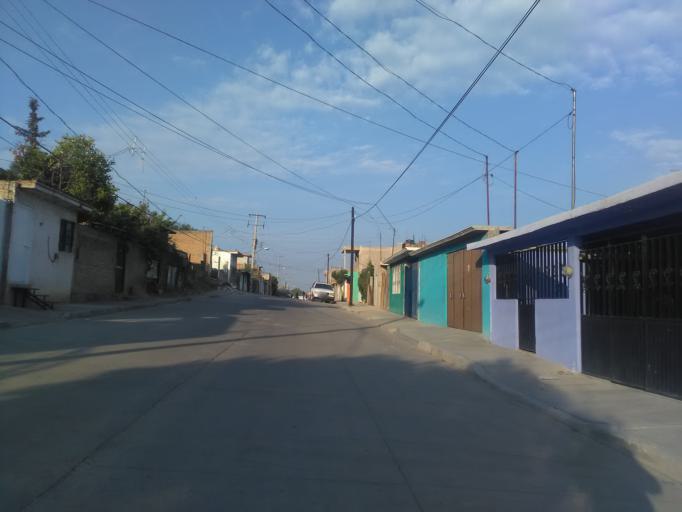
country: MX
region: Durango
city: Victoria de Durango
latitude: 24.0477
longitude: -104.6493
